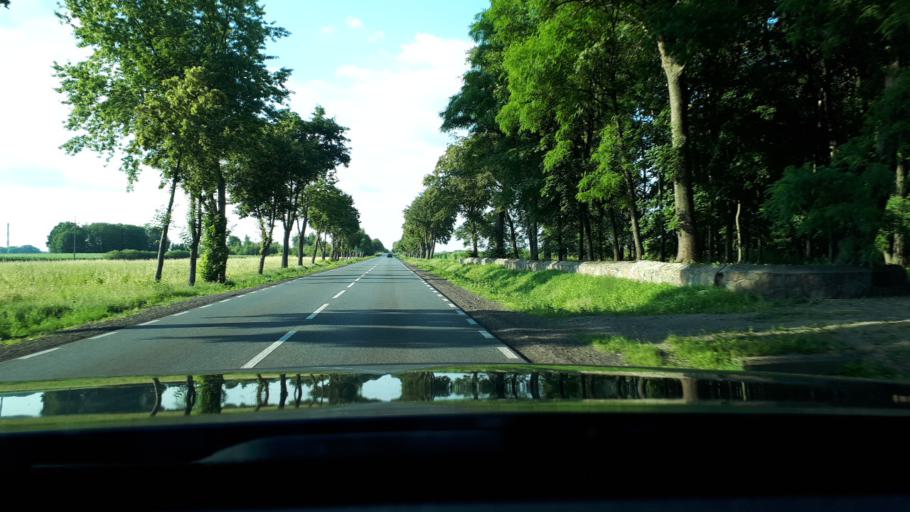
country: PL
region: Masovian Voivodeship
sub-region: Powiat ciechanowski
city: Ciechanow
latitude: 52.8316
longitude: 20.6189
